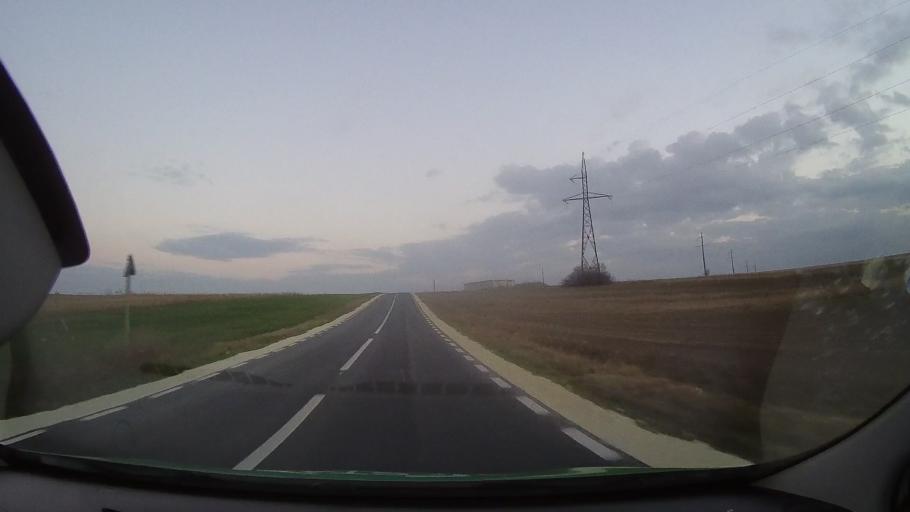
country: RO
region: Constanta
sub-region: Comuna Baneasa
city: Baneasa
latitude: 44.1048
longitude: 27.6726
